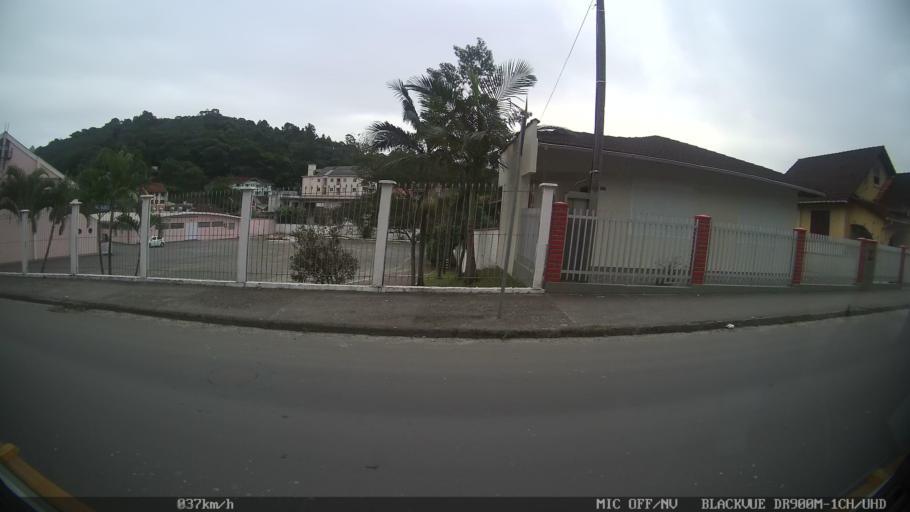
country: BR
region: Santa Catarina
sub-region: Joinville
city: Joinville
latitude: -26.2945
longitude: -48.8729
